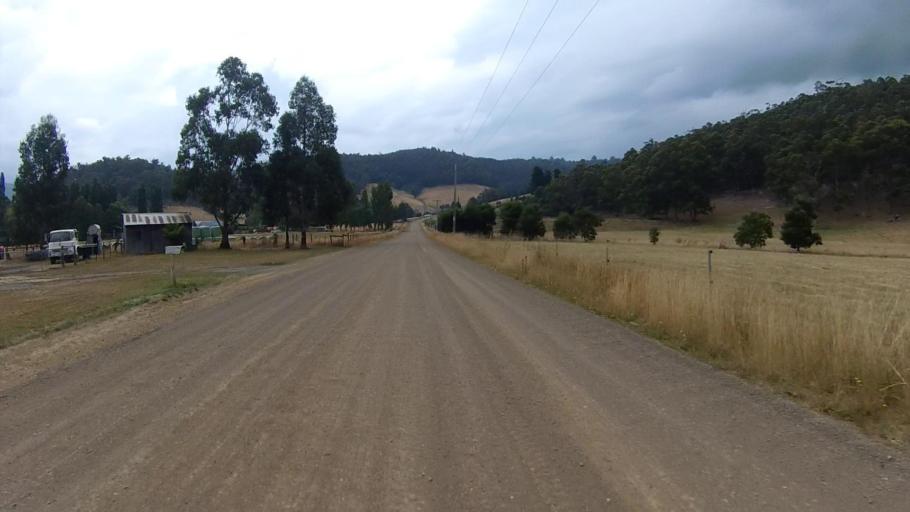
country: AU
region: Tasmania
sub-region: Huon Valley
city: Huonville
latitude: -42.9778
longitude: 147.0551
